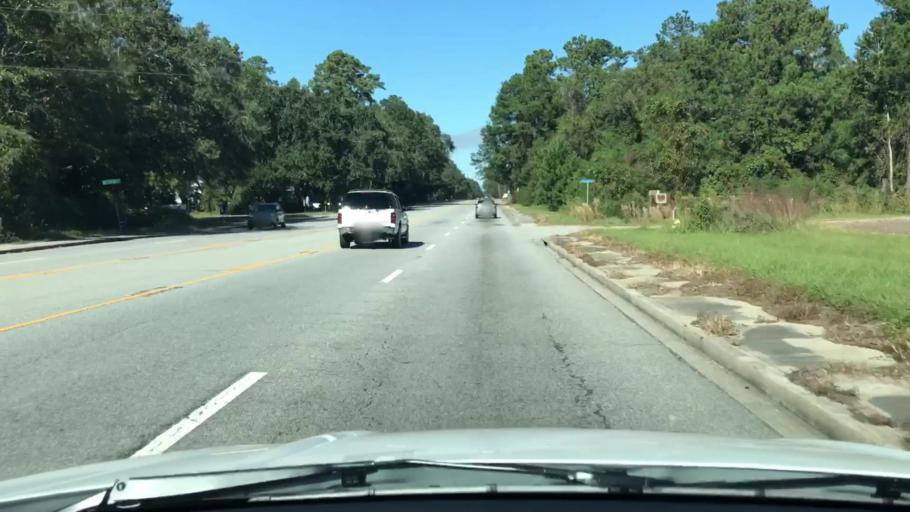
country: US
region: South Carolina
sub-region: Beaufort County
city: Laurel Bay
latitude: 32.5521
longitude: -80.7439
